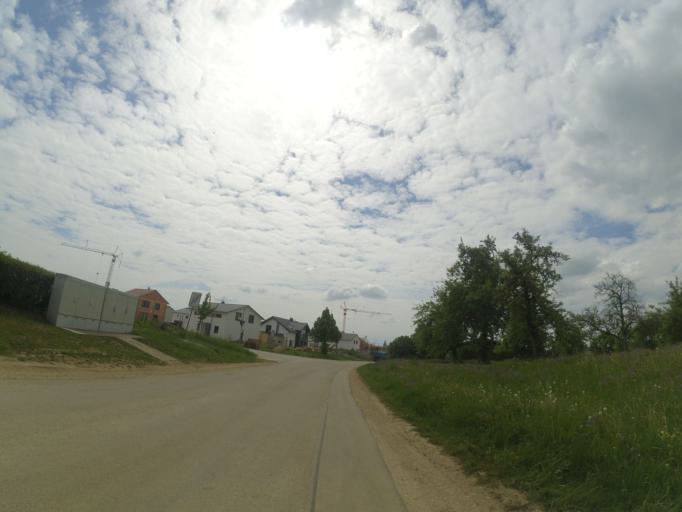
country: DE
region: Baden-Wuerttemberg
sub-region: Tuebingen Region
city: Berghulen
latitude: 48.4608
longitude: 9.7609
